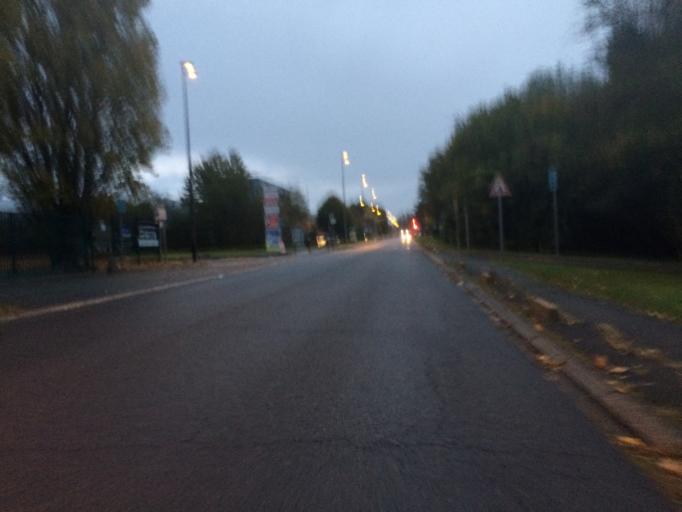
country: FR
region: Ile-de-France
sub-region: Departement de l'Essonne
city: Orsay
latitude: 48.6885
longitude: 2.2036
